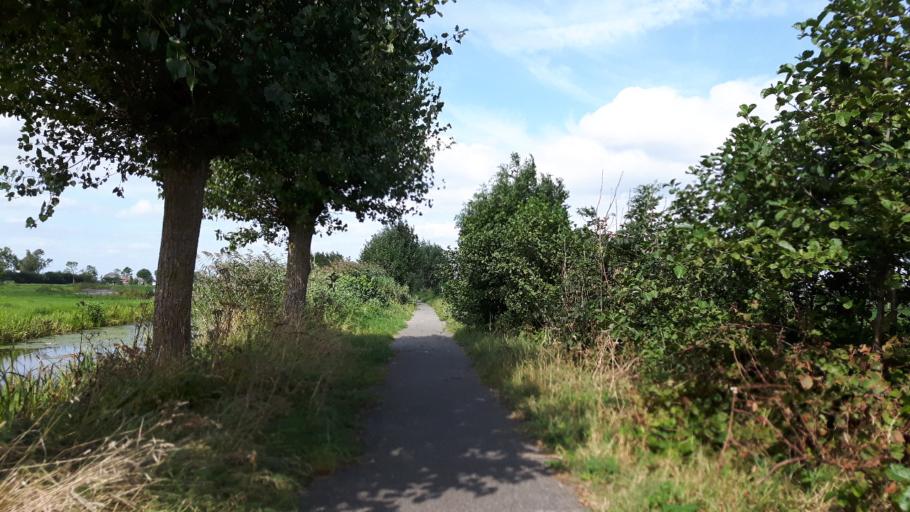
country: NL
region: Utrecht
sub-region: Gemeente Woerden
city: Woerden
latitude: 52.1223
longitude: 4.8387
